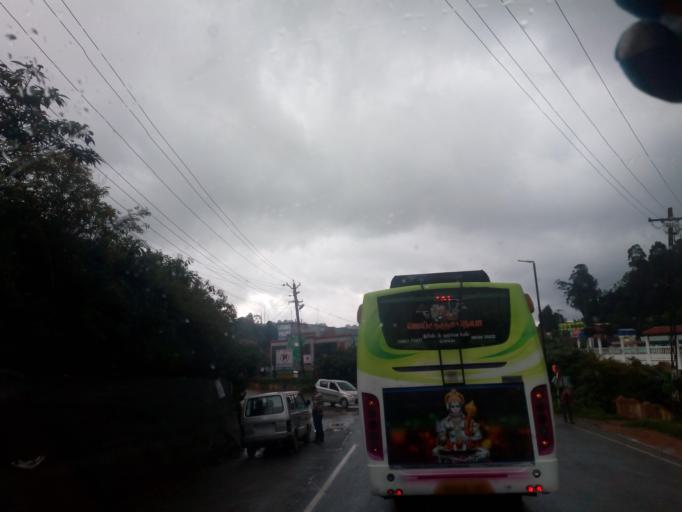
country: IN
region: Tamil Nadu
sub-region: Nilgiri
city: Ooty
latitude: 11.4135
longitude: 76.7102
